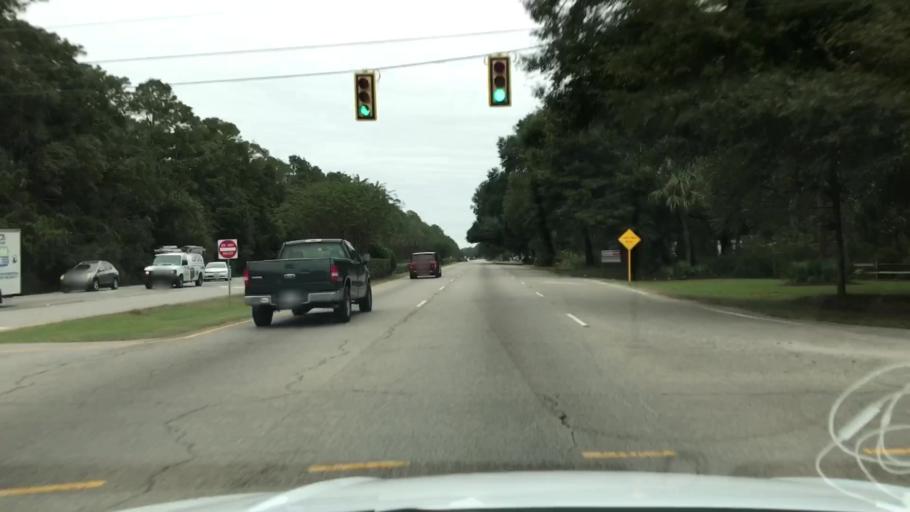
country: US
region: South Carolina
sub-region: Georgetown County
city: Murrells Inlet
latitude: 33.4909
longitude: -79.0904
